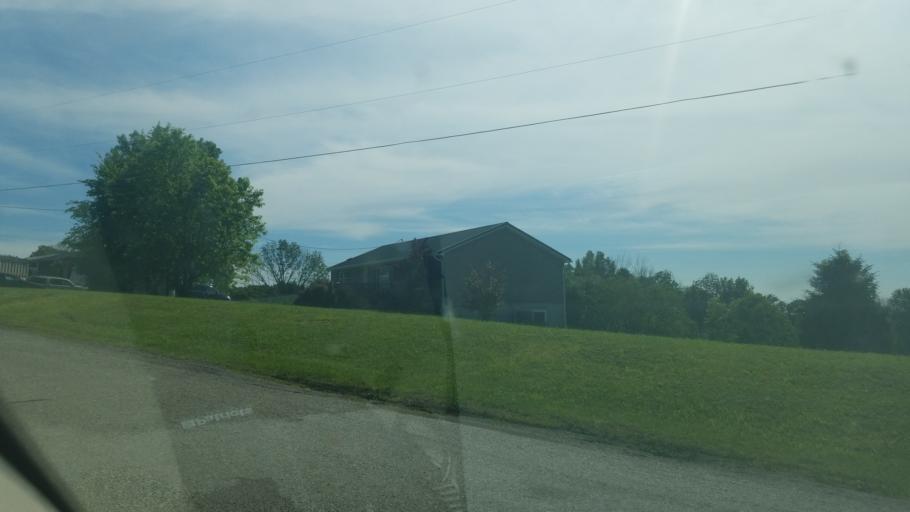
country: US
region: Ohio
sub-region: Holmes County
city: Millersburg
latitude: 40.4901
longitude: -81.9663
